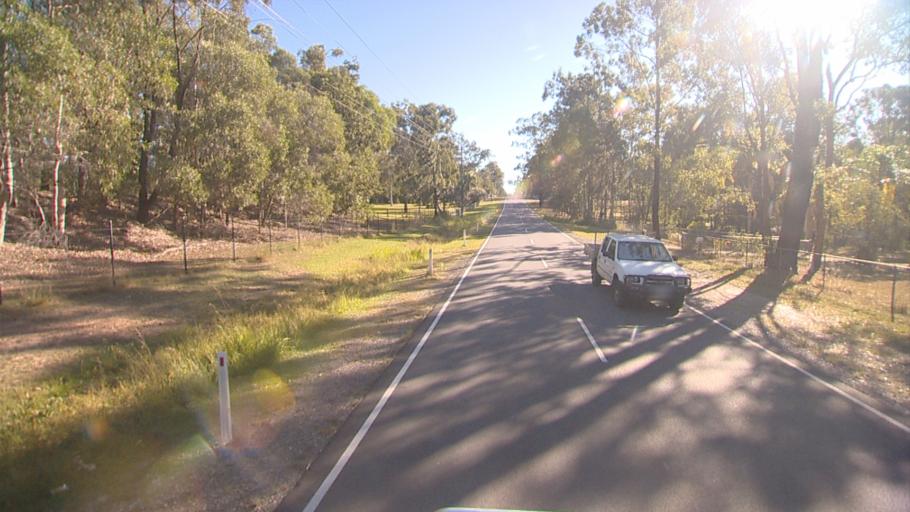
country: AU
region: Queensland
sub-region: Logan
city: Park Ridge South
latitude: -27.7365
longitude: 153.0231
